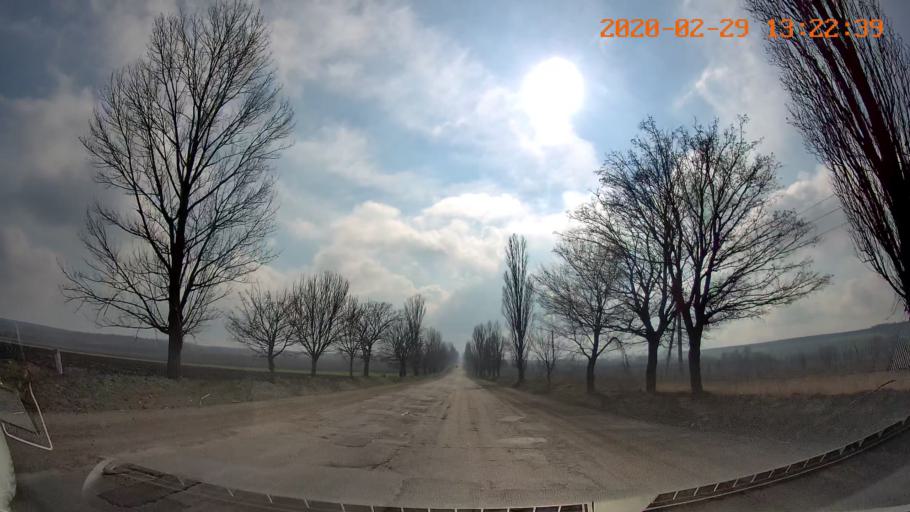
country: MD
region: Telenesti
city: Camenca
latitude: 47.9580
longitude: 28.6274
